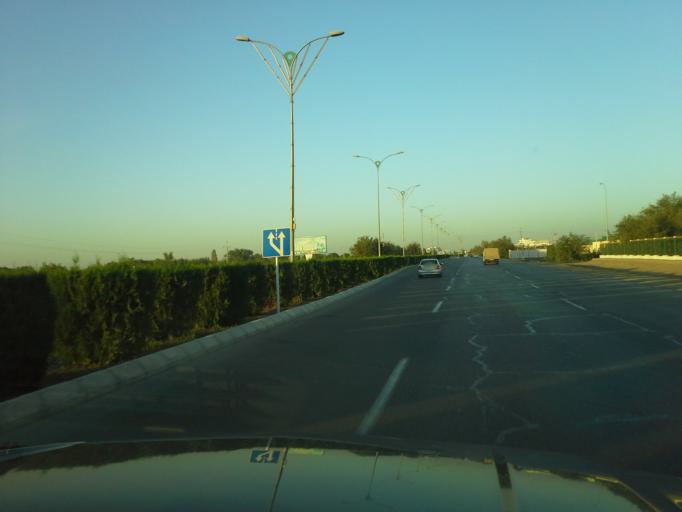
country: TM
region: Dasoguz
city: Dasoguz
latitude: 41.8084
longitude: 59.9082
